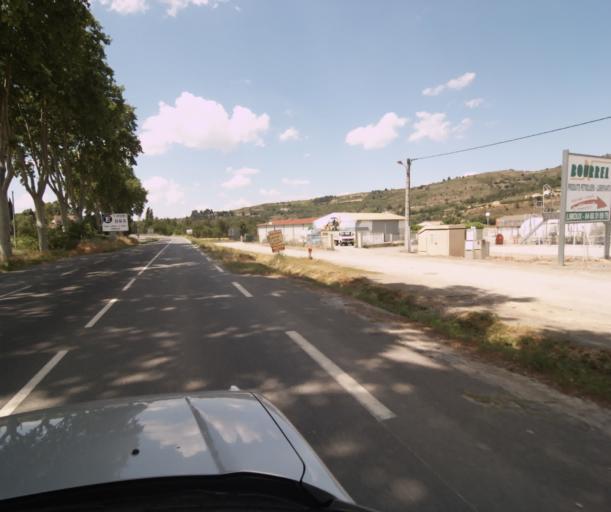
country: FR
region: Languedoc-Roussillon
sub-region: Departement de l'Aude
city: Limoux
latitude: 43.0418
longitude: 2.2403
